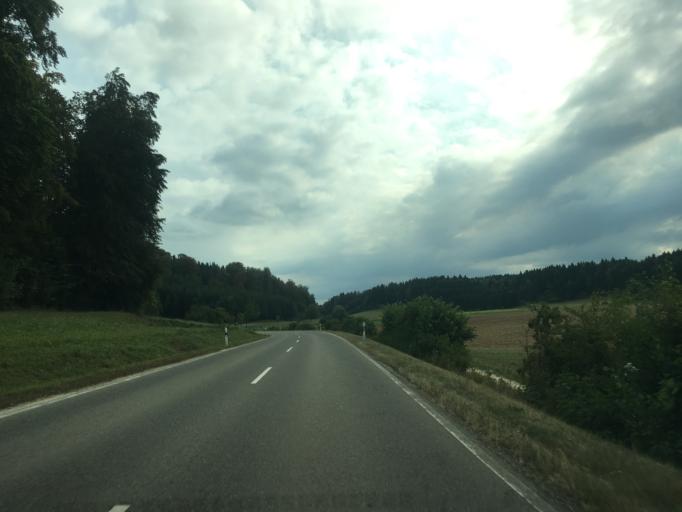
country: DE
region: Baden-Wuerttemberg
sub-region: Tuebingen Region
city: Hayingen
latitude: 48.3356
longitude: 9.4340
